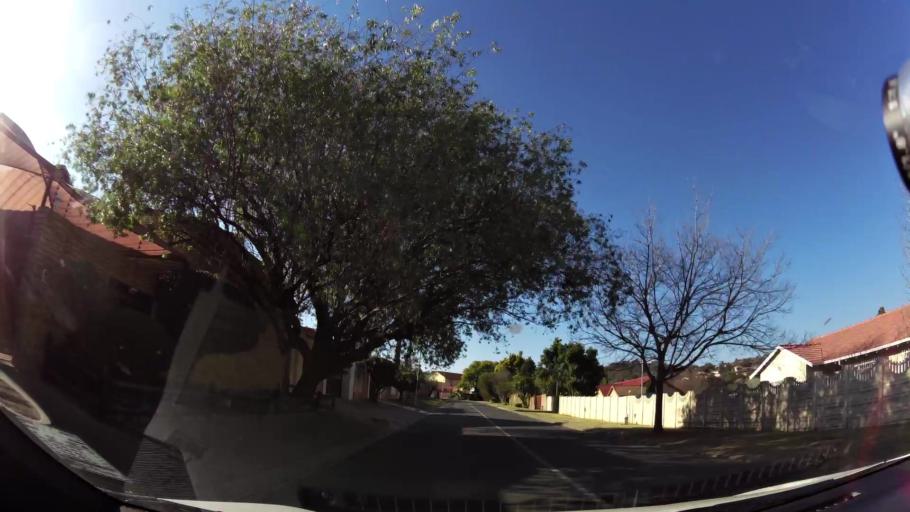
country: ZA
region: Gauteng
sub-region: City of Johannesburg Metropolitan Municipality
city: Johannesburg
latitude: -26.2917
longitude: 28.0505
